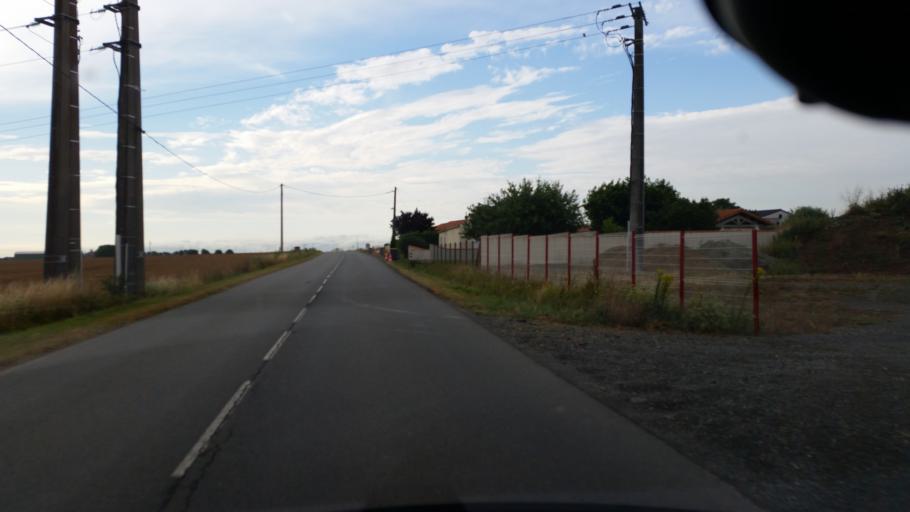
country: FR
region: Poitou-Charentes
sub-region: Departement de la Charente-Maritime
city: Marans
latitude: 46.3014
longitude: -0.9825
